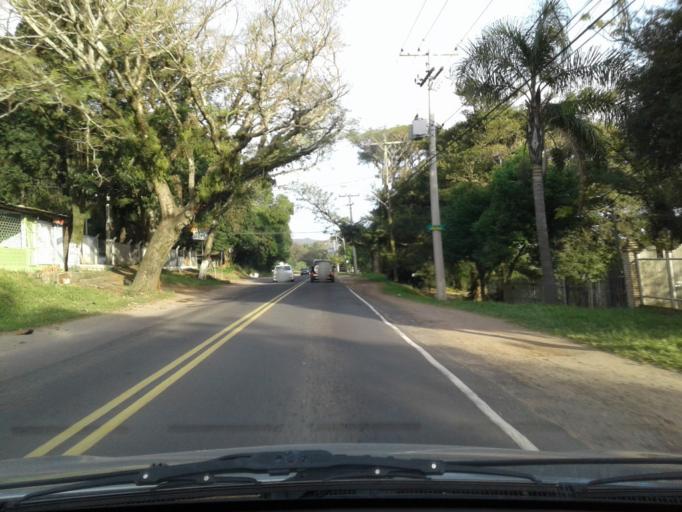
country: BR
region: Rio Grande do Sul
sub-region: Porto Alegre
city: Porto Alegre
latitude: -30.1090
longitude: -51.2202
